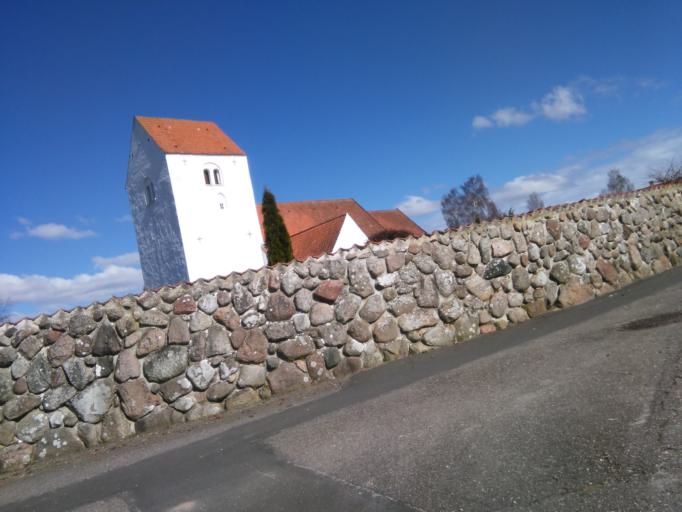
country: DK
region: Central Jutland
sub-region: Horsens Kommune
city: Horsens
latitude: 55.8921
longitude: 10.0038
